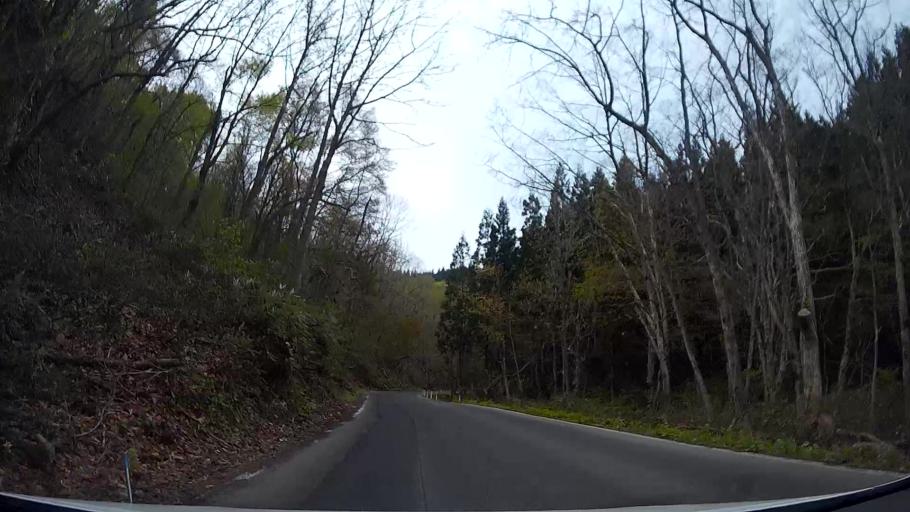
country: JP
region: Akita
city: Hanawa
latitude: 40.3812
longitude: 140.8907
